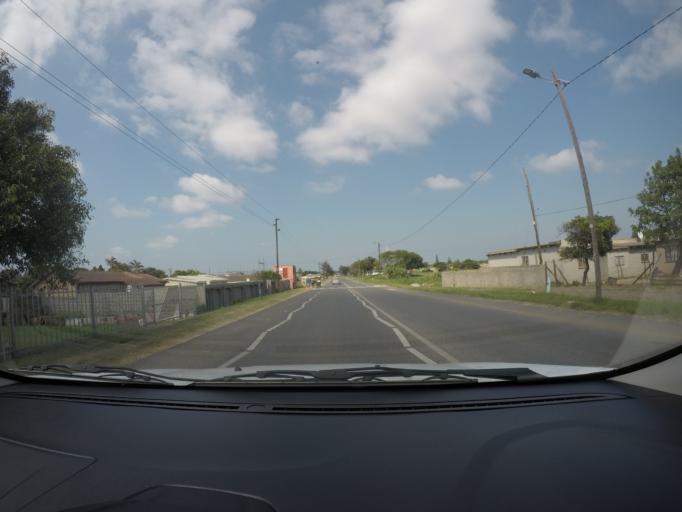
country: ZA
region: KwaZulu-Natal
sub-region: uThungulu District Municipality
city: eSikhawini
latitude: -28.8844
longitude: 31.9019
